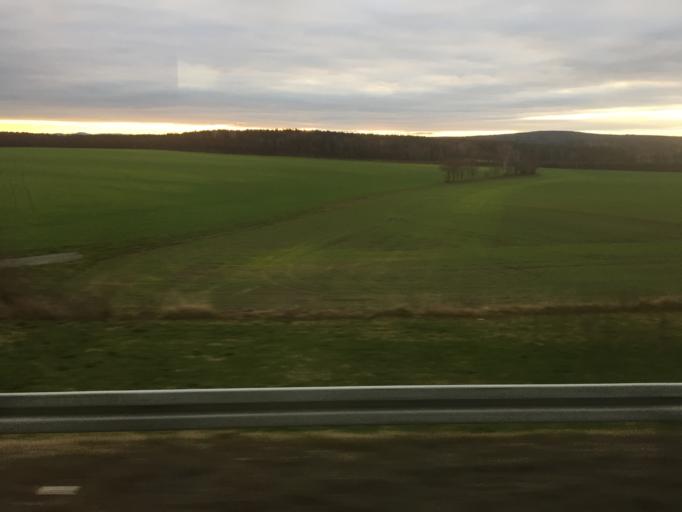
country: DE
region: Brandenburg
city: Grosskmehlen
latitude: 51.3572
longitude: 13.7293
